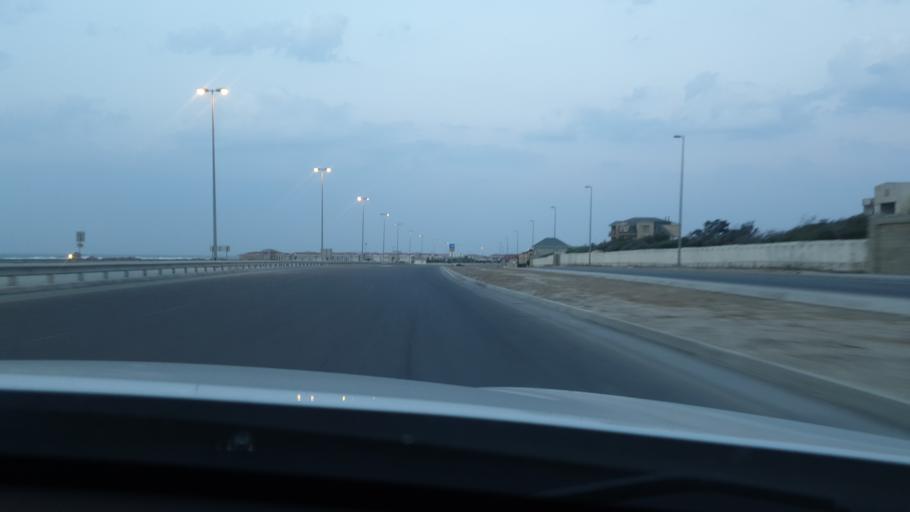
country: AZ
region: Baki
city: Bilajer
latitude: 40.5888
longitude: 50.0503
